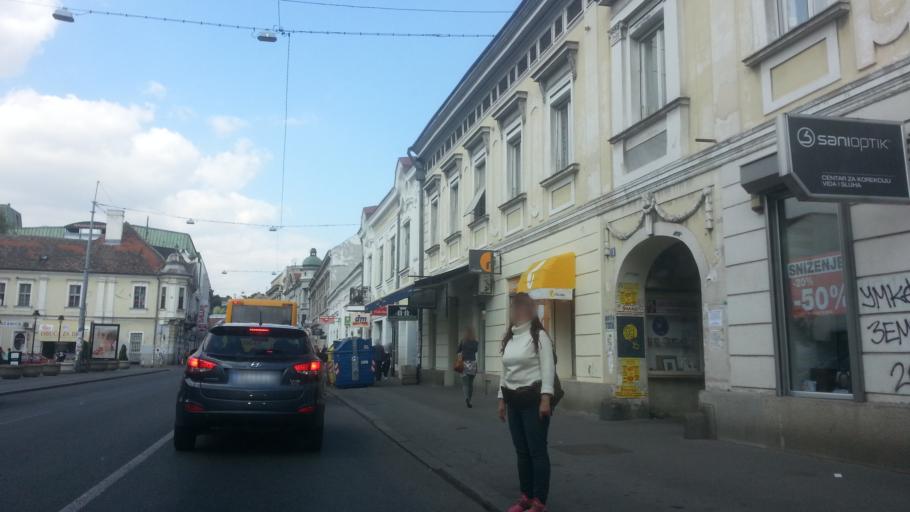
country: RS
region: Central Serbia
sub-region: Belgrade
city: Zemun
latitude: 44.8437
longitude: 20.4120
